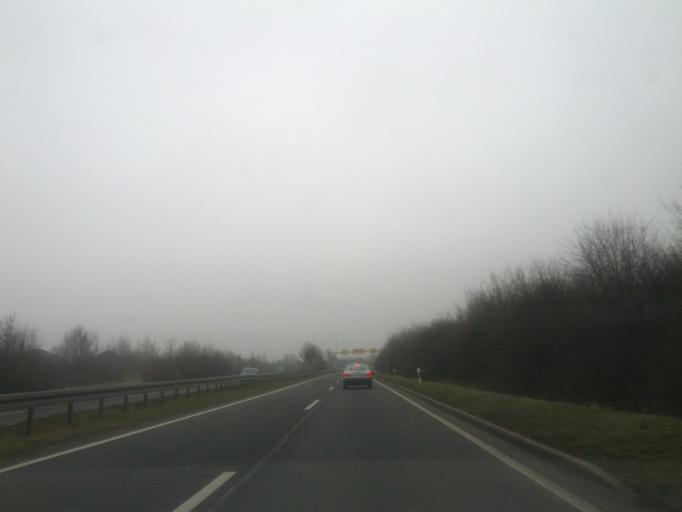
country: DE
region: Thuringia
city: Erfurt
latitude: 50.9647
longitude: 11.0893
